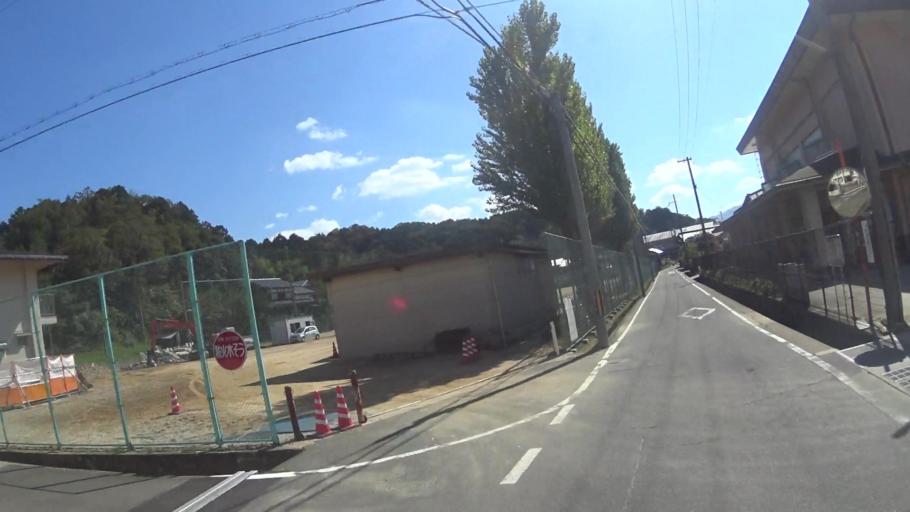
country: JP
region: Hyogo
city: Toyooka
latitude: 35.5920
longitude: 134.9316
